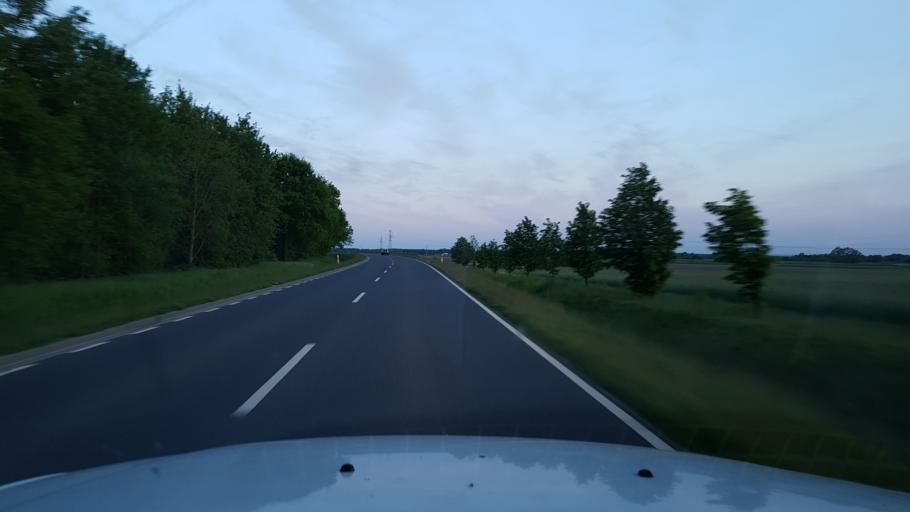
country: PL
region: West Pomeranian Voivodeship
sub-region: Powiat goleniowski
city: Goleniow
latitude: 53.5822
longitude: 14.8681
